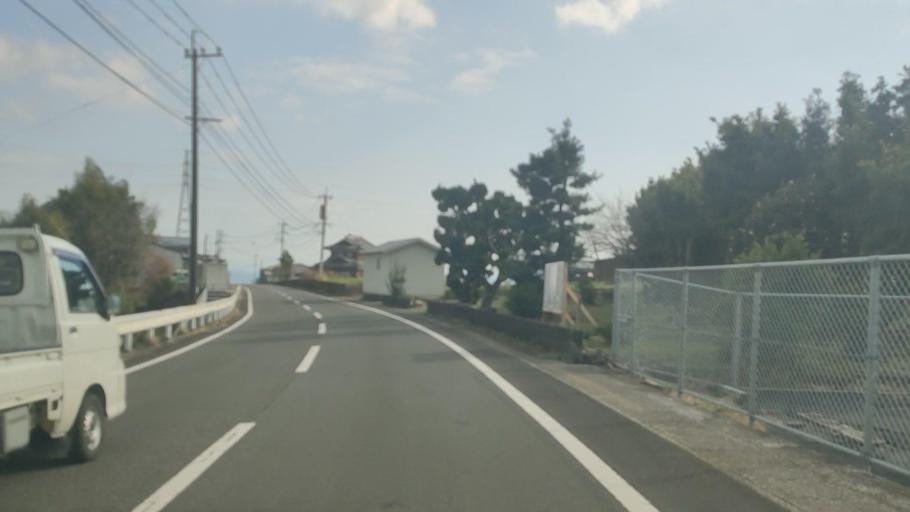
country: JP
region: Nagasaki
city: Shimabara
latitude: 32.6706
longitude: 130.2833
